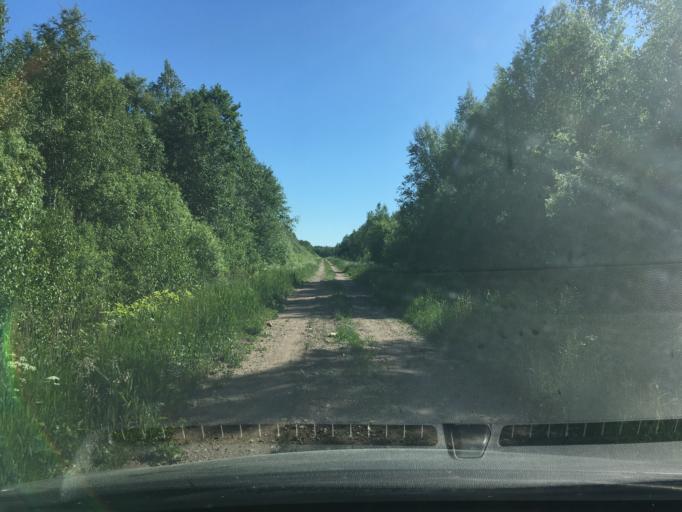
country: EE
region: Laeaene
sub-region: Lihula vald
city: Lihula
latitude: 58.6275
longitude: 23.7291
